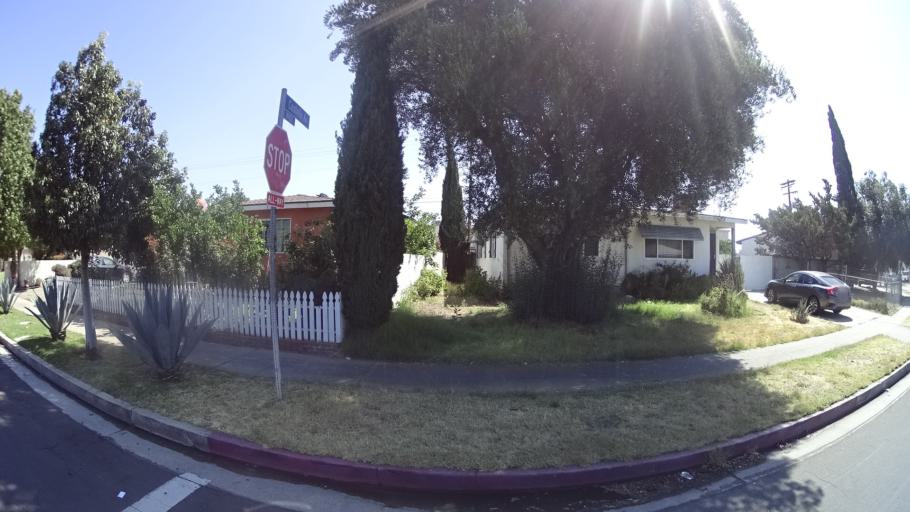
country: US
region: California
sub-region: Los Angeles County
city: Van Nuys
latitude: 34.2328
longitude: -118.4405
